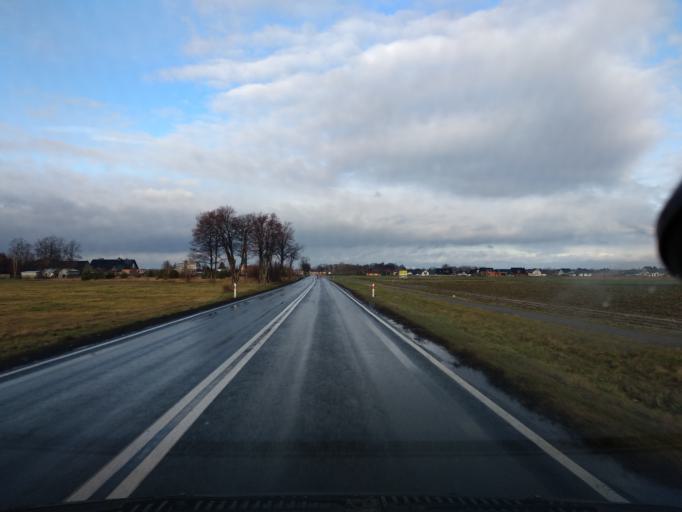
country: PL
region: Greater Poland Voivodeship
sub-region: Powiat koninski
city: Rychwal
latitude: 52.0578
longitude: 18.1635
